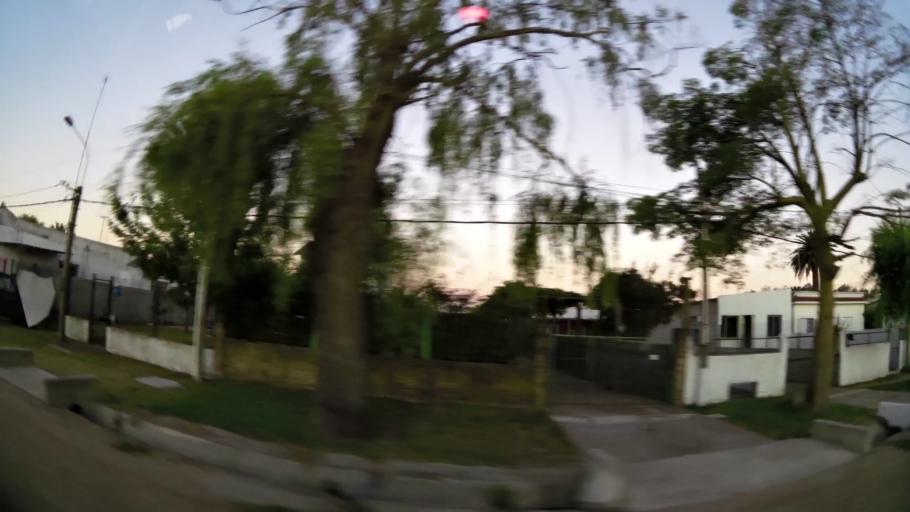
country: UY
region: Canelones
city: Toledo
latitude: -34.8105
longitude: -56.1400
